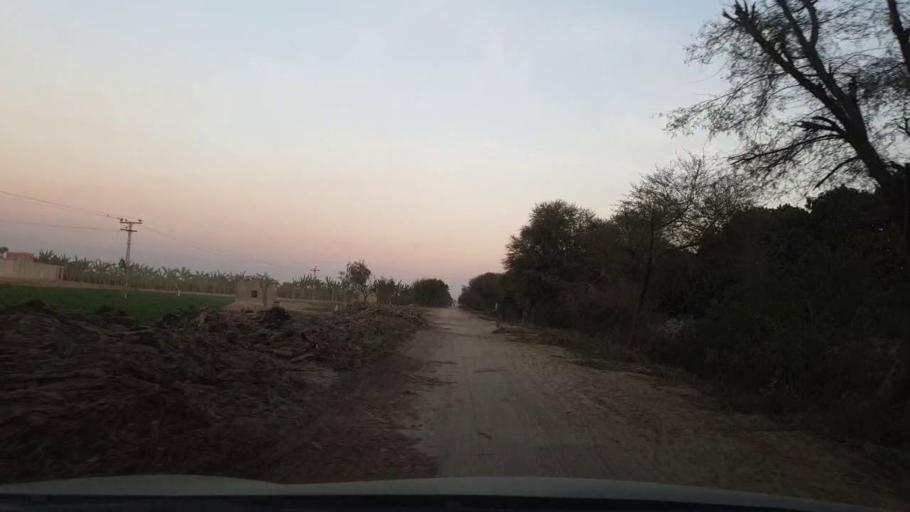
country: PK
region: Sindh
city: Tando Allahyar
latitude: 25.5608
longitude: 68.7723
